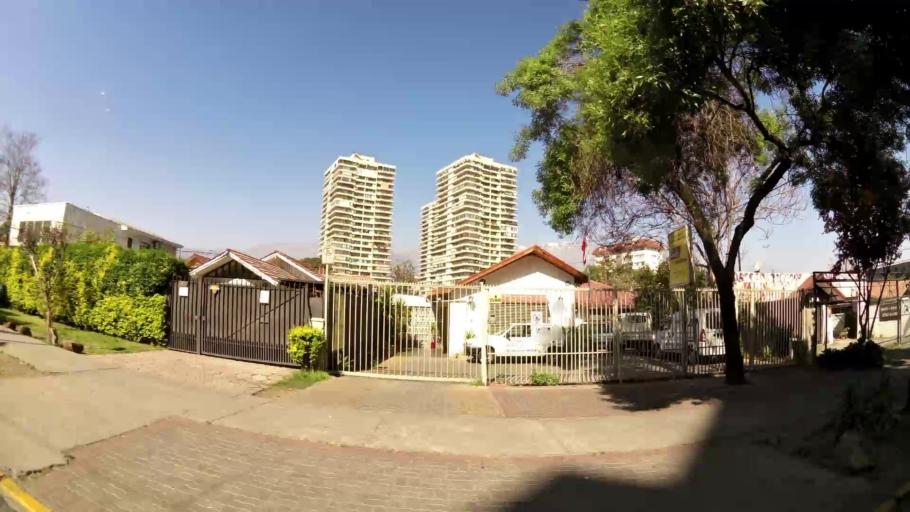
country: CL
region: Santiago Metropolitan
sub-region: Provincia de Santiago
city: Villa Presidente Frei, Nunoa, Santiago, Chile
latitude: -33.4069
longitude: -70.5510
